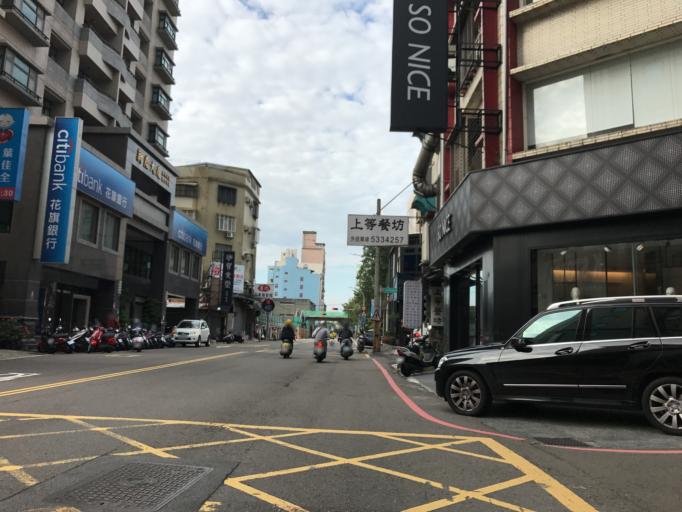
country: TW
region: Taiwan
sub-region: Hsinchu
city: Hsinchu
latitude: 24.8102
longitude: 120.9735
